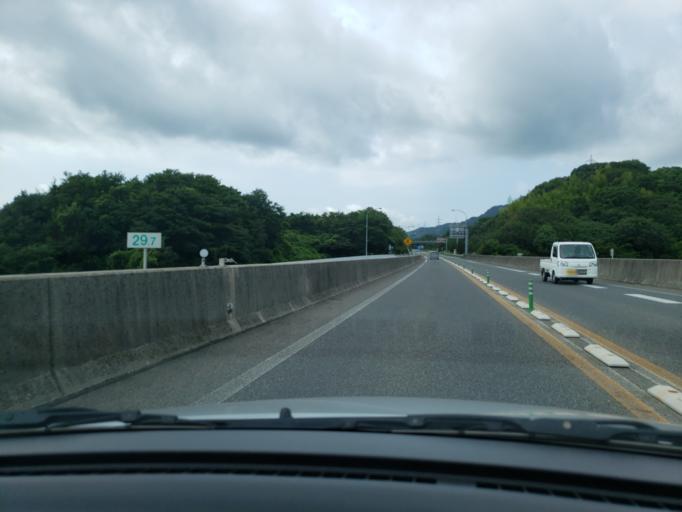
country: JP
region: Hiroshima
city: Innoshima
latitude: 34.2486
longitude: 133.0486
